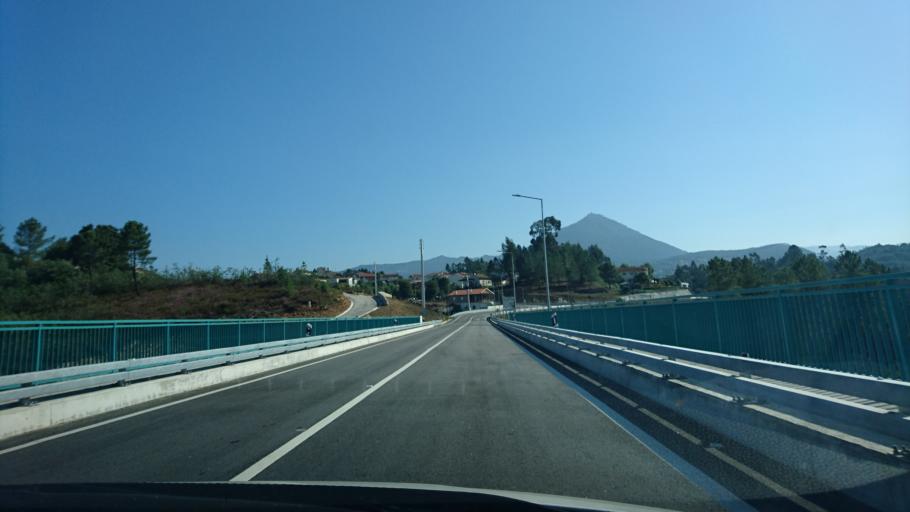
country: PT
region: Vila Real
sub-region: Mondim de Basto
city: Mondim de Basto
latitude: 41.4098
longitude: -7.9758
